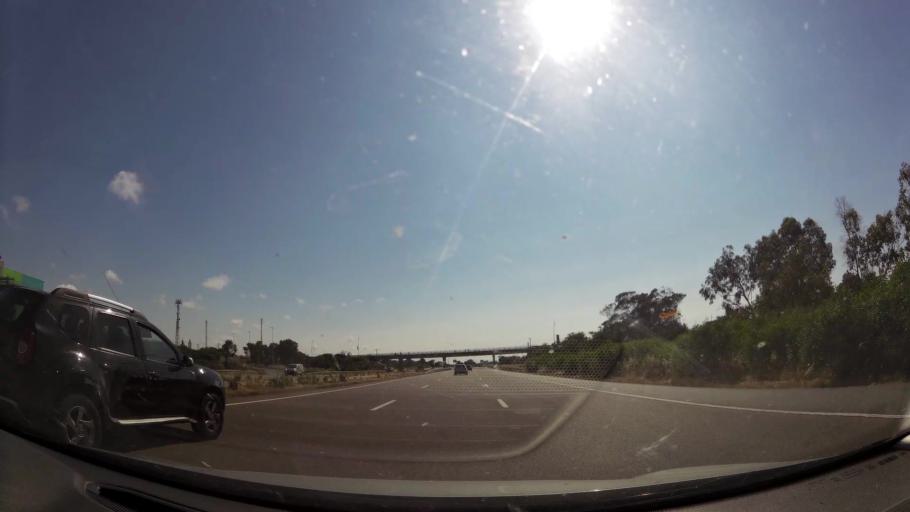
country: MA
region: Chaouia-Ouardigha
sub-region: Benslimane
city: Bouznika
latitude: 33.8011
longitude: -7.1577
